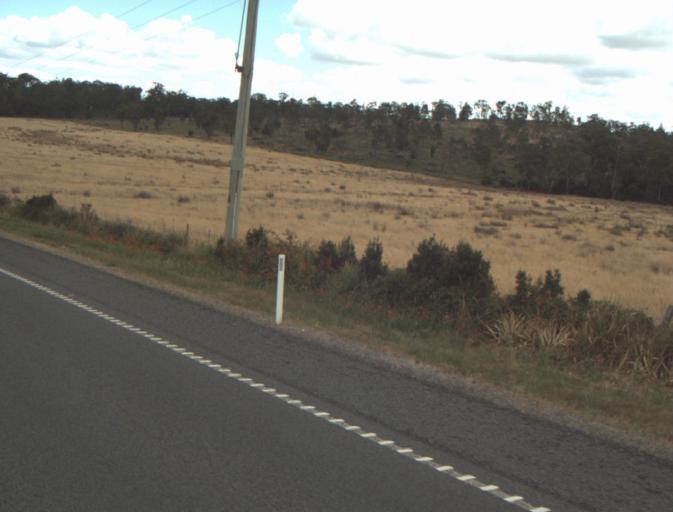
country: AU
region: Tasmania
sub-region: Launceston
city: Mayfield
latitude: -41.2517
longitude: 147.0223
